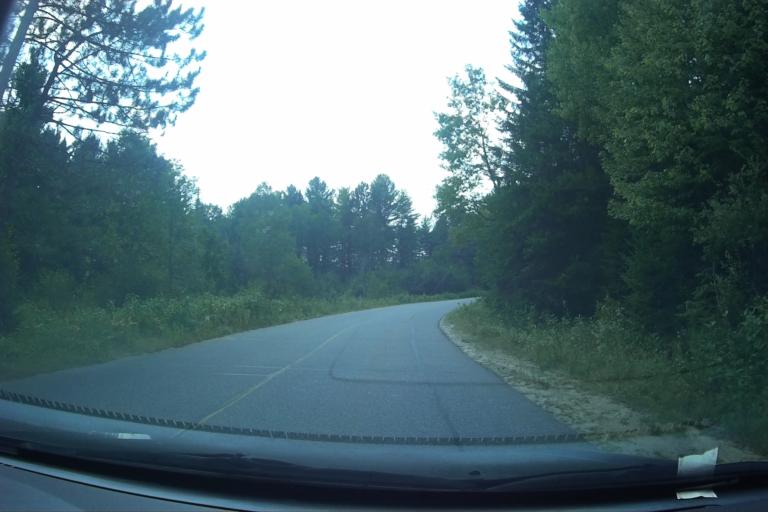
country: CA
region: Ontario
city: Bancroft
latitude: 45.5876
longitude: -78.3650
